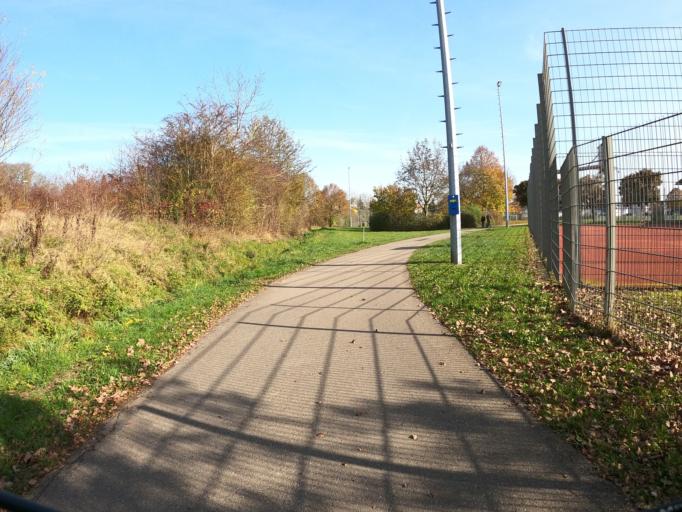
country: DE
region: Bavaria
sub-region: Swabia
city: Nersingen
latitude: 48.4506
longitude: 10.0954
